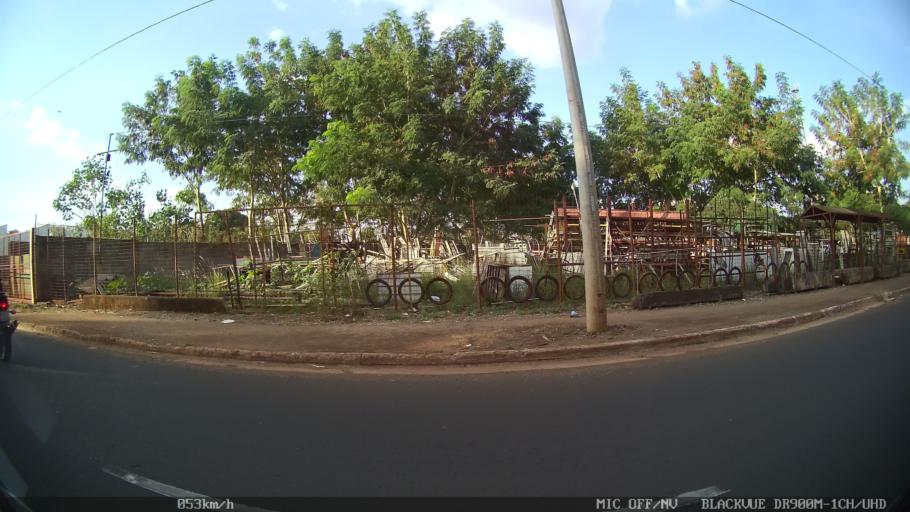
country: BR
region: Sao Paulo
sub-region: Ribeirao Preto
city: Ribeirao Preto
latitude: -21.1426
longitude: -47.8024
